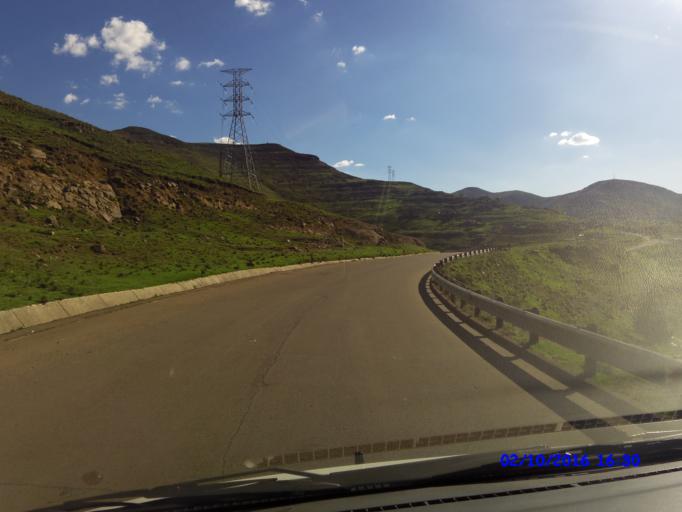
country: LS
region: Maseru
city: Nako
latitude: -29.4794
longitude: 28.0803
